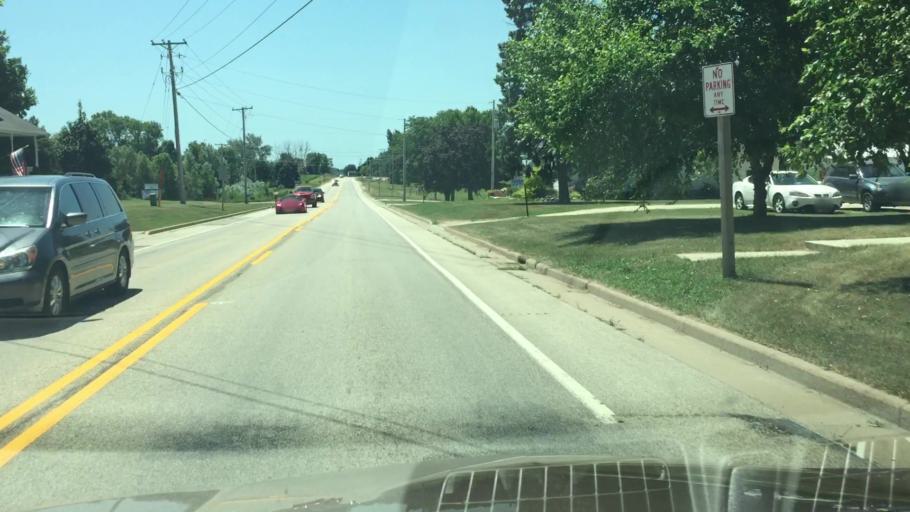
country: US
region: Wisconsin
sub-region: Fond du Lac County
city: Saint Peter
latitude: 43.9344
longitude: -88.3039
